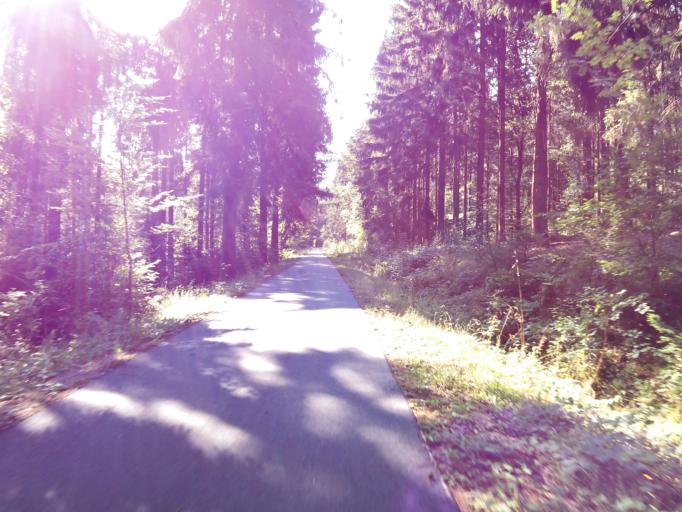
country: DE
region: Baden-Wuerttemberg
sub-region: Karlsruhe Region
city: Mudau
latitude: 49.5072
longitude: 9.2145
